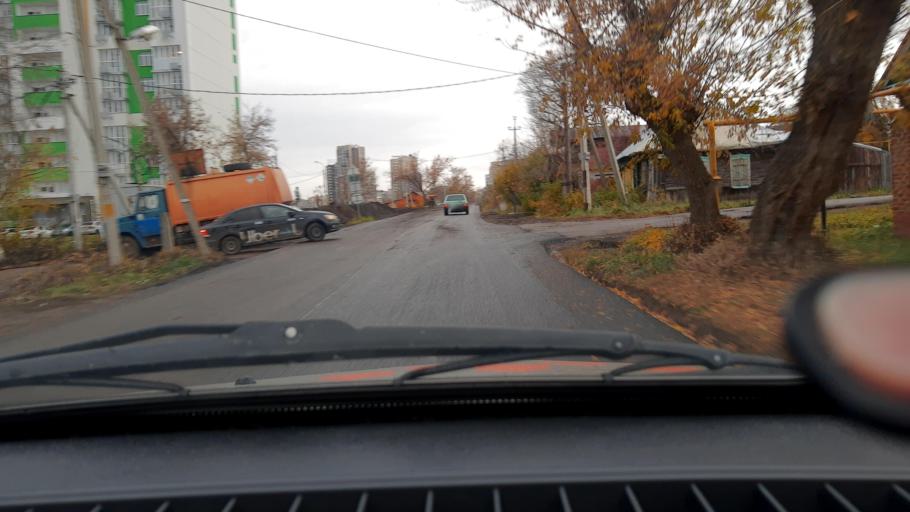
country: RU
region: Bashkortostan
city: Ufa
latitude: 54.7234
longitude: 55.9737
